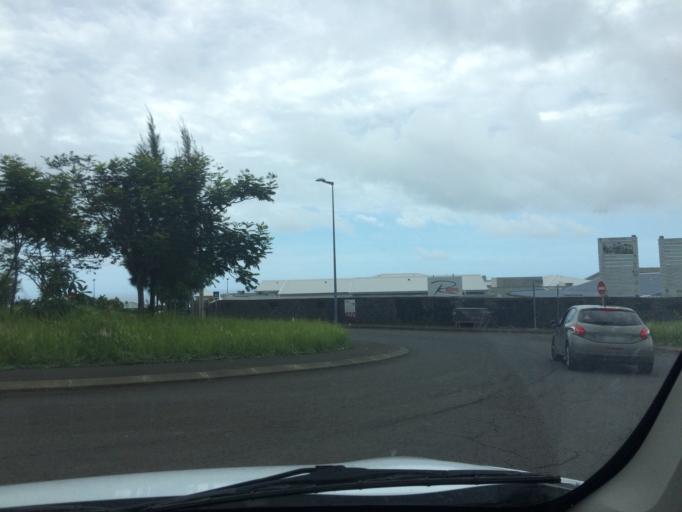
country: RE
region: Reunion
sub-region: Reunion
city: Saint-Pierre
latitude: -21.3364
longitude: 55.4878
